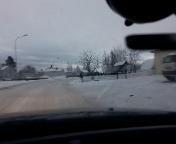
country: SE
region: Gaevleborg
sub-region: Bollnas Kommun
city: Bollnas
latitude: 61.3554
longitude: 16.3876
